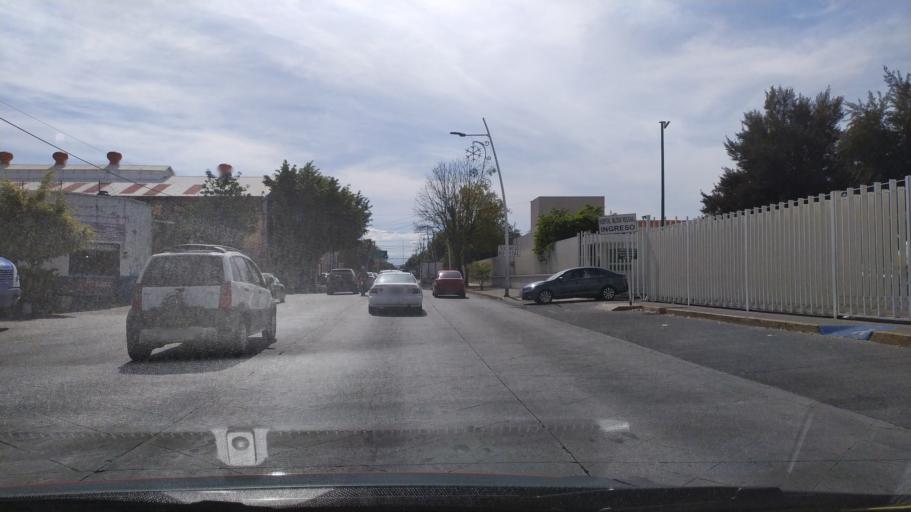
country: MX
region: Jalisco
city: Tlaquepaque
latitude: 20.6684
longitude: -103.3319
